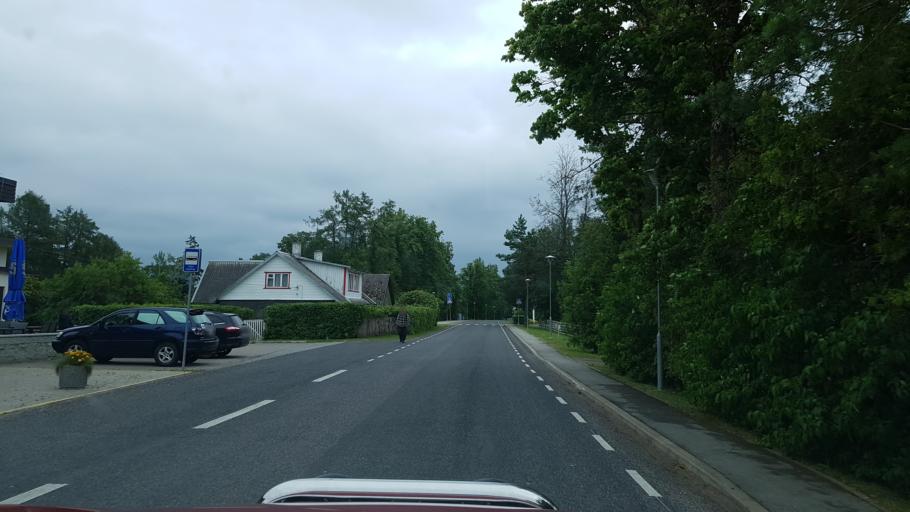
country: EE
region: Ida-Virumaa
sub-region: Toila vald
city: Toila
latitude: 59.4188
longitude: 27.5109
